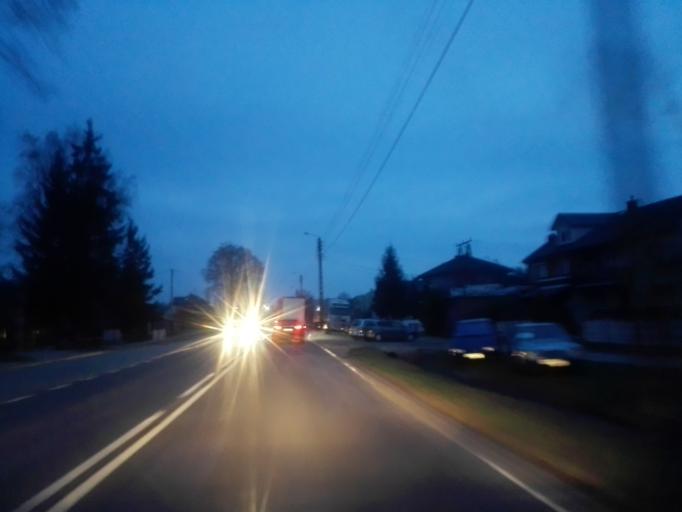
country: PL
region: Podlasie
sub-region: Lomza
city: Lomza
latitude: 53.1409
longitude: 22.0442
